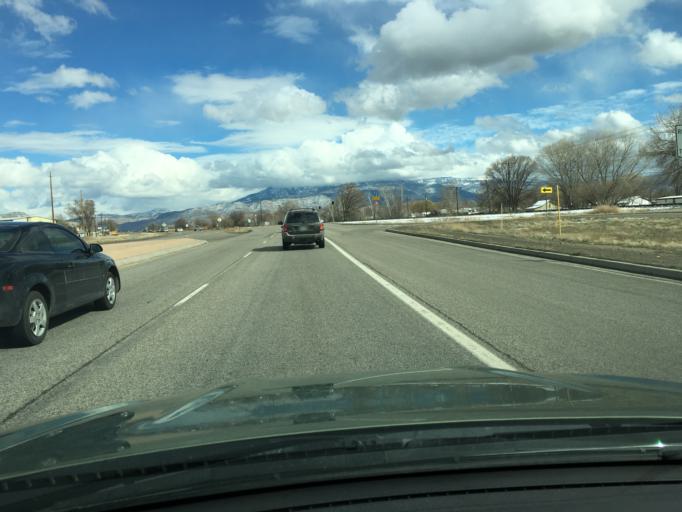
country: US
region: Colorado
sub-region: Mesa County
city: Fruitvale
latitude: 39.0778
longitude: -108.4948
